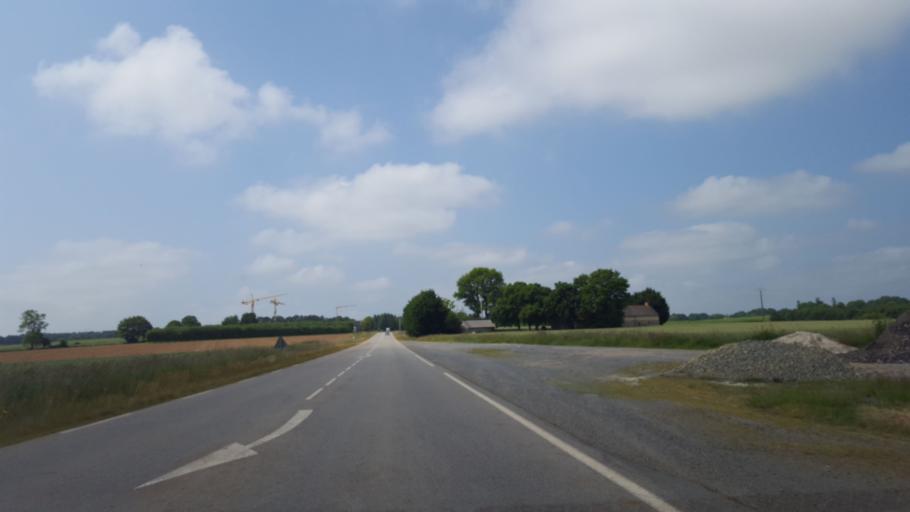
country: FR
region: Brittany
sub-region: Departement d'Ille-et-Vilaine
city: Maure-de-Bretagne
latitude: 47.9159
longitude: -1.9729
